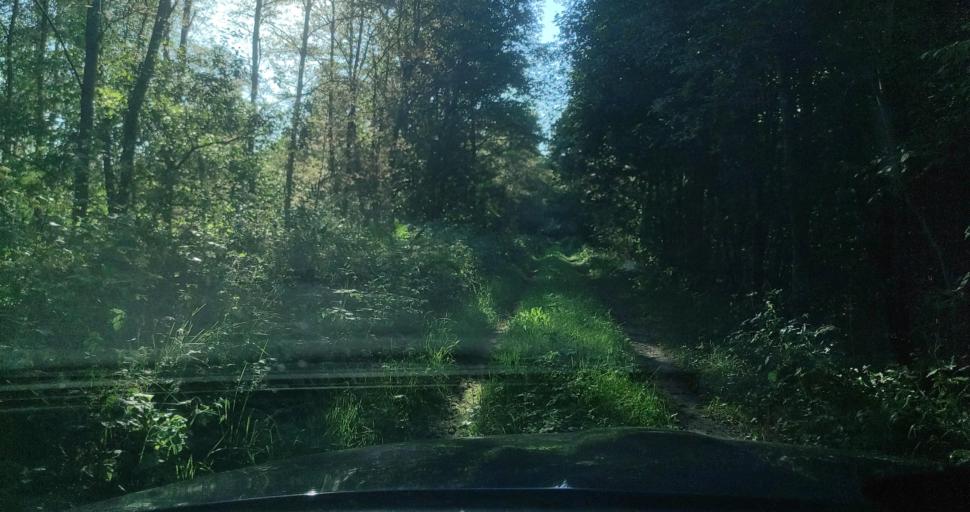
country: LV
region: Skrunda
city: Skrunda
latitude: 56.6793
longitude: 21.9784
